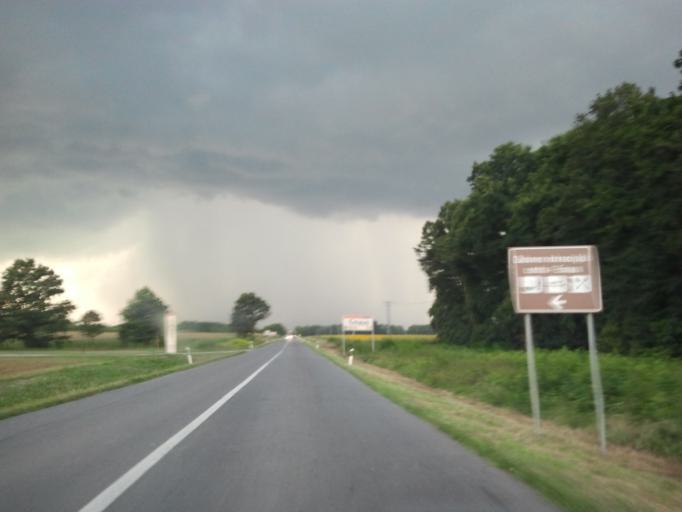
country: HR
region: Osjecko-Baranjska
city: Ladimirevci
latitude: 45.6296
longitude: 18.4913
